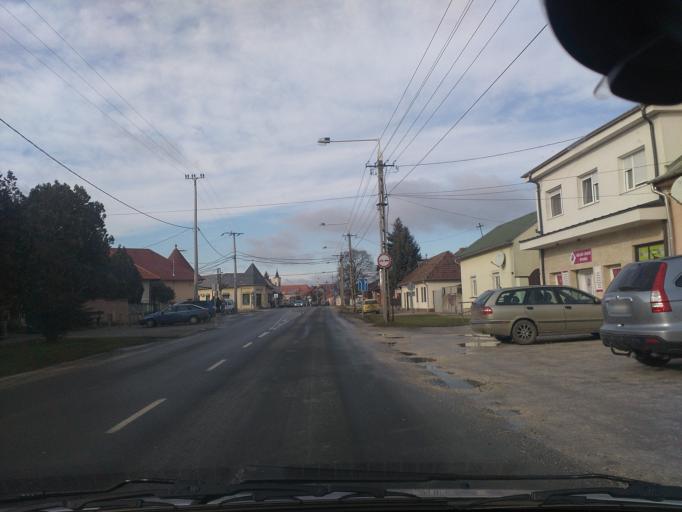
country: HU
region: Komarom-Esztergom
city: Tat
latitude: 47.7423
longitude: 18.6492
